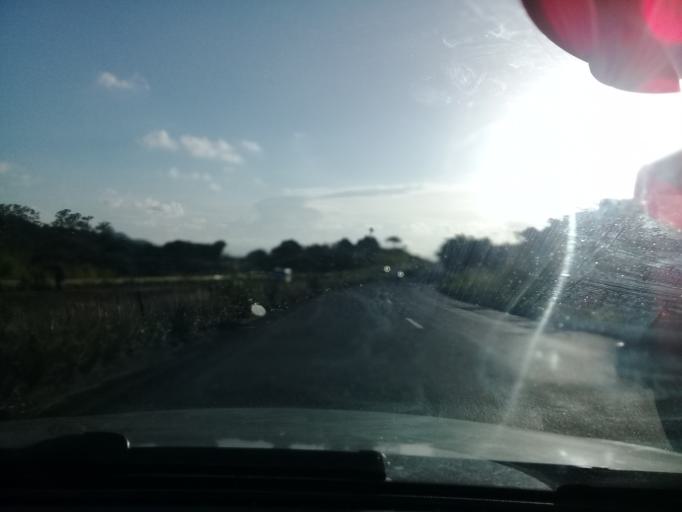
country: BR
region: Pernambuco
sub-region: Moreno
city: Moreno
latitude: -8.1135
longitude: -35.1123
